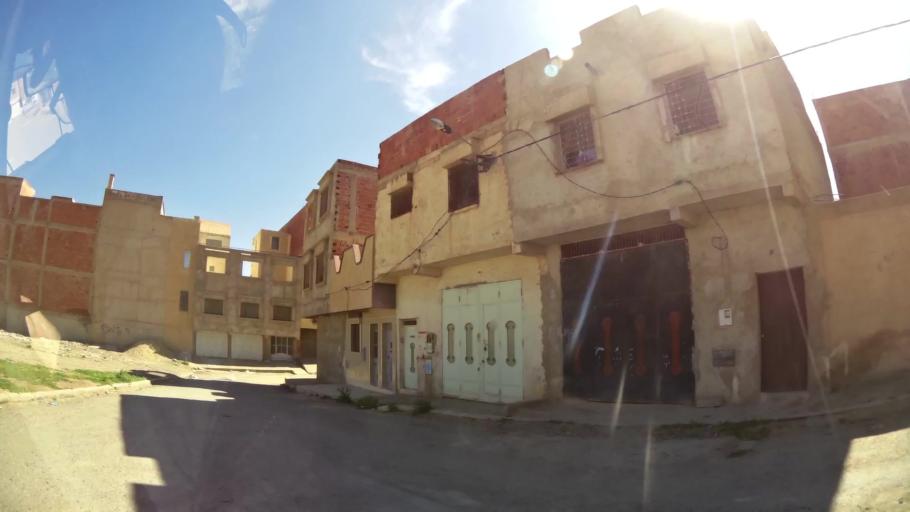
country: MA
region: Oriental
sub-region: Oujda-Angad
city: Oujda
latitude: 34.6566
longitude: -1.9369
